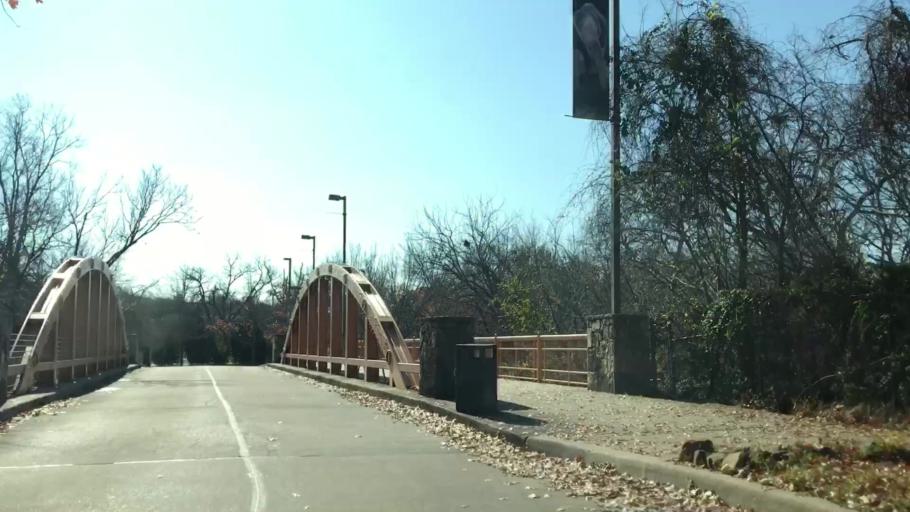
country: US
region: Texas
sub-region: Dallas County
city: Dallas
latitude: 32.7423
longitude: -96.8139
